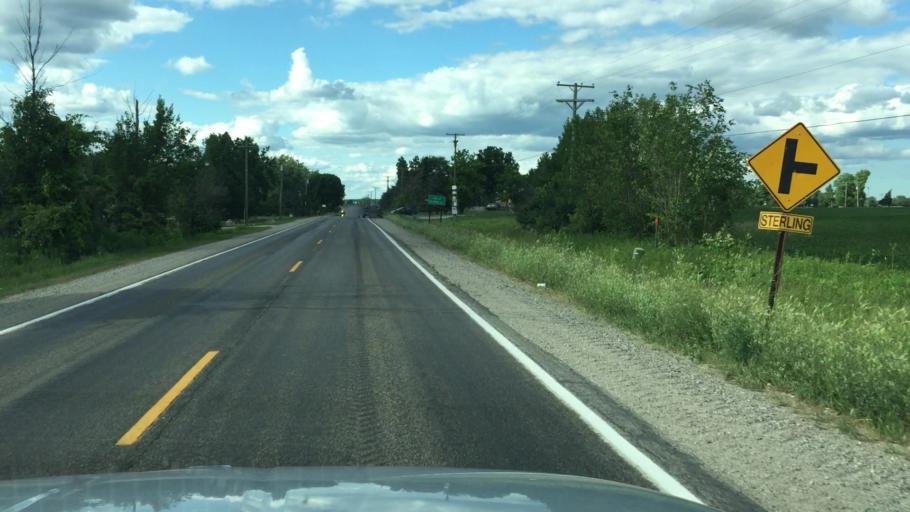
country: US
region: Michigan
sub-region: Saint Clair County
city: Capac
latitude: 43.0639
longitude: -82.9300
